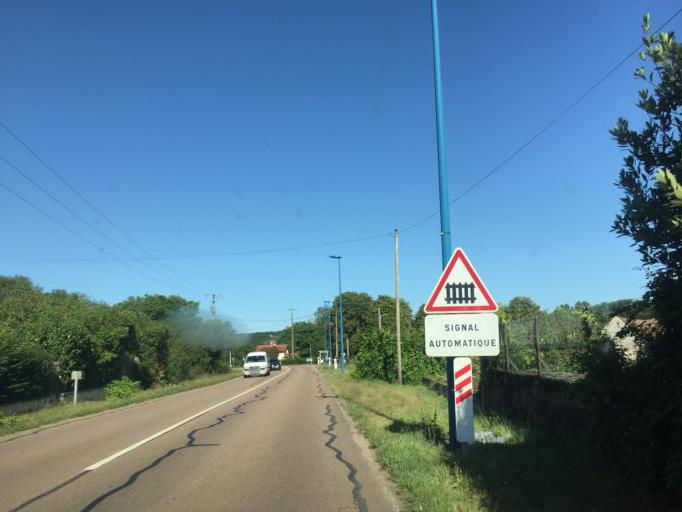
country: FR
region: Bourgogne
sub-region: Departement de la Nievre
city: Clamecy
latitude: 47.4482
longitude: 3.4910
